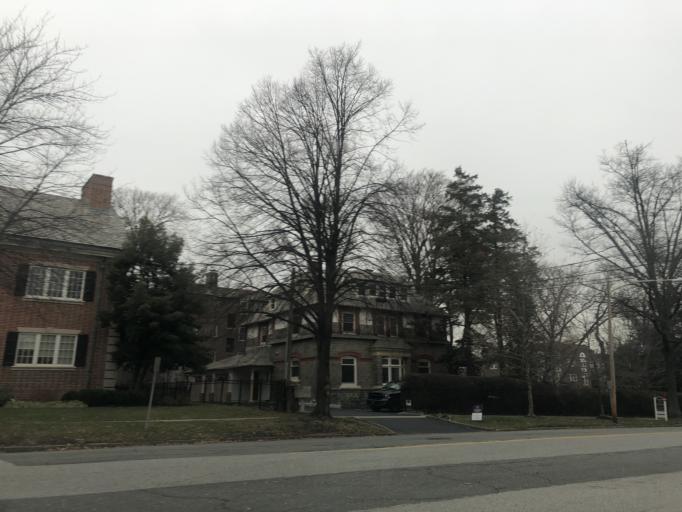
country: US
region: Pennsylvania
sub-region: Montgomery County
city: Bryn Mawr
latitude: 40.0224
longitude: -75.3154
